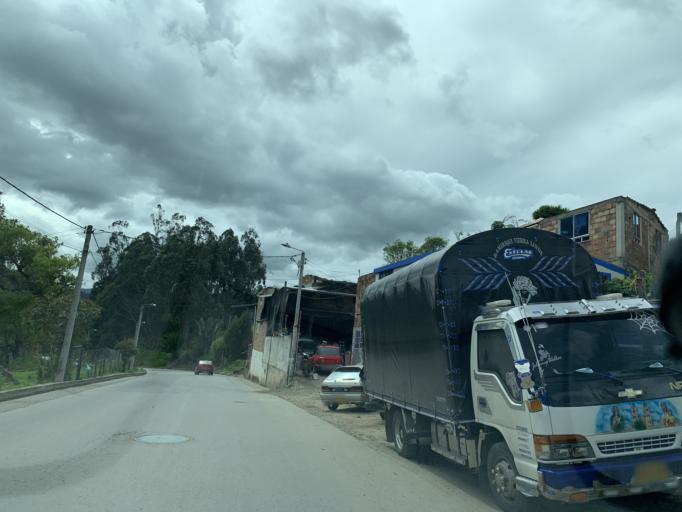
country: CO
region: Boyaca
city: Ramiriqui
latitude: 5.4065
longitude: -73.3326
